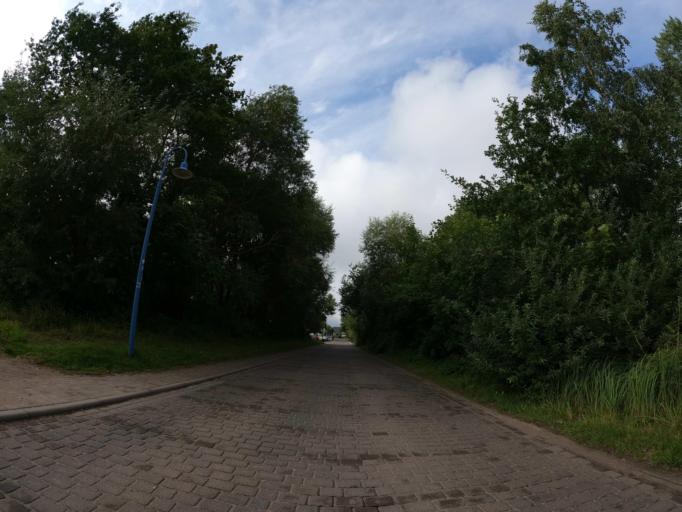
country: DE
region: Mecklenburg-Vorpommern
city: Ostseebad Gohren
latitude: 54.3204
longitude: 13.7246
